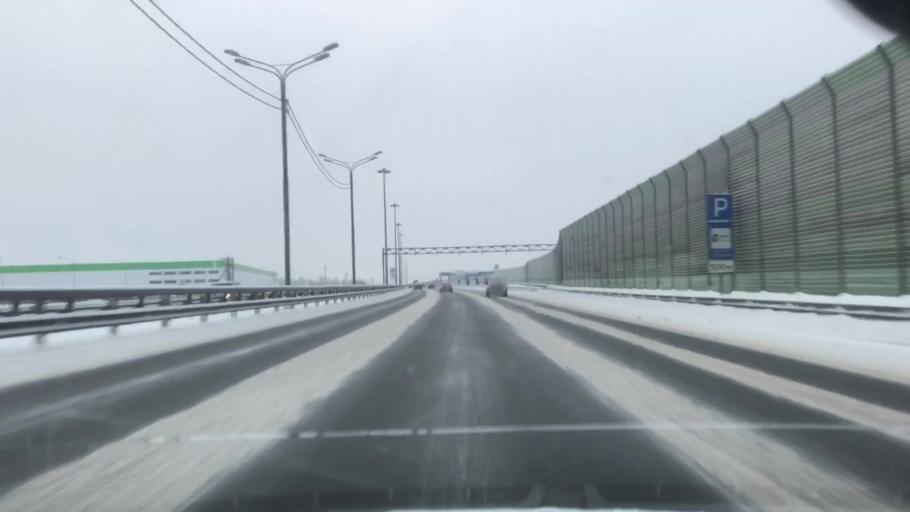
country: RU
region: Moskovskaya
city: Belyye Stolby
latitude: 55.3293
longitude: 37.8103
